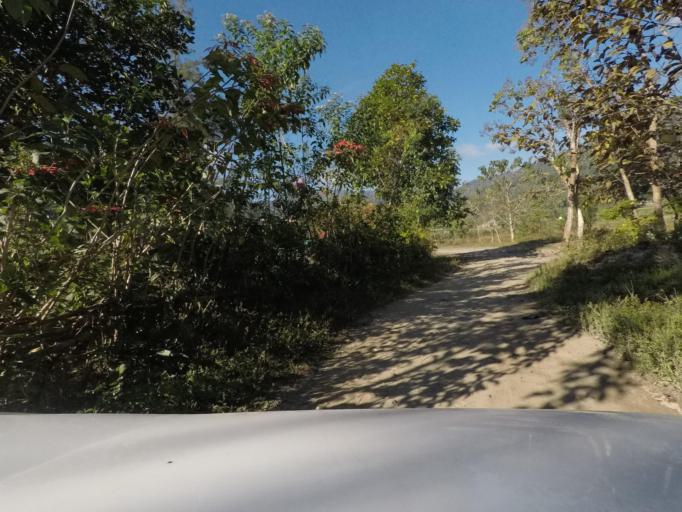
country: TL
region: Ermera
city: Gleno
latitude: -8.7336
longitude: 125.4313
